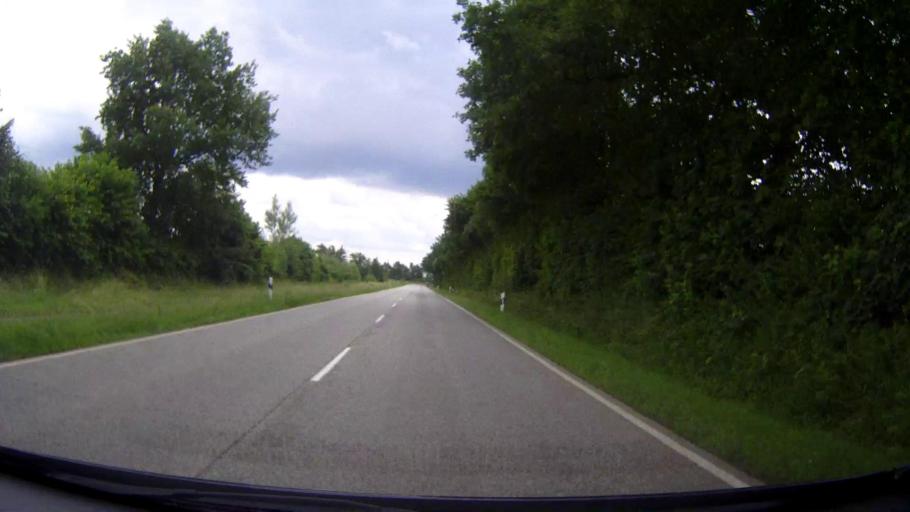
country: DE
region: Schleswig-Holstein
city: Warringholz
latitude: 54.0661
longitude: 9.4725
